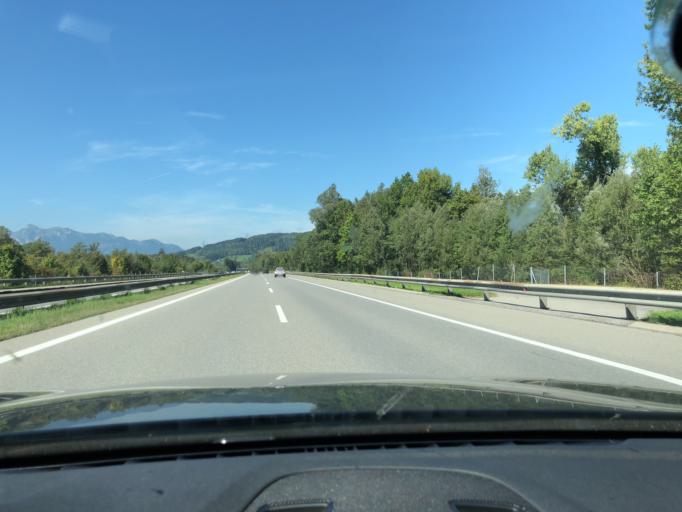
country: AT
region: Vorarlberg
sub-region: Politischer Bezirk Feldkirch
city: Satteins
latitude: 47.2077
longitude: 9.6684
